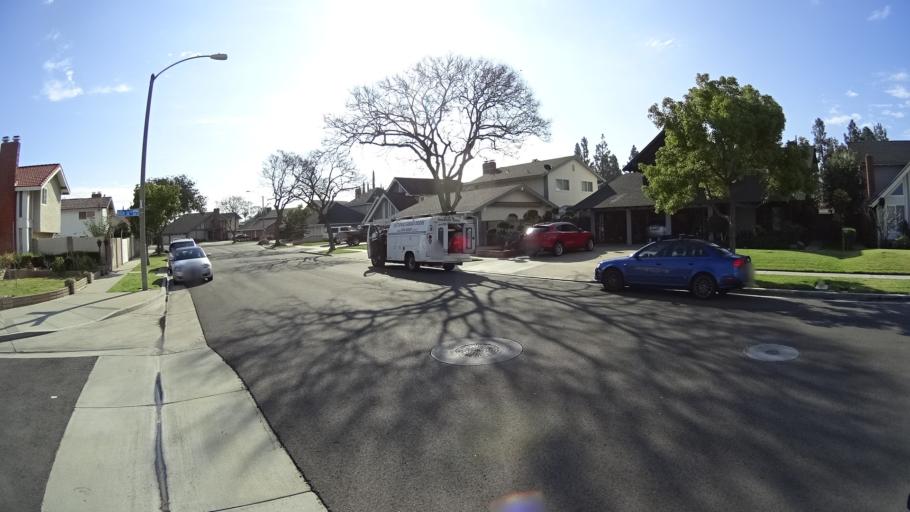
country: US
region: California
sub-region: Orange County
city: Placentia
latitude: 33.8409
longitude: -117.8780
